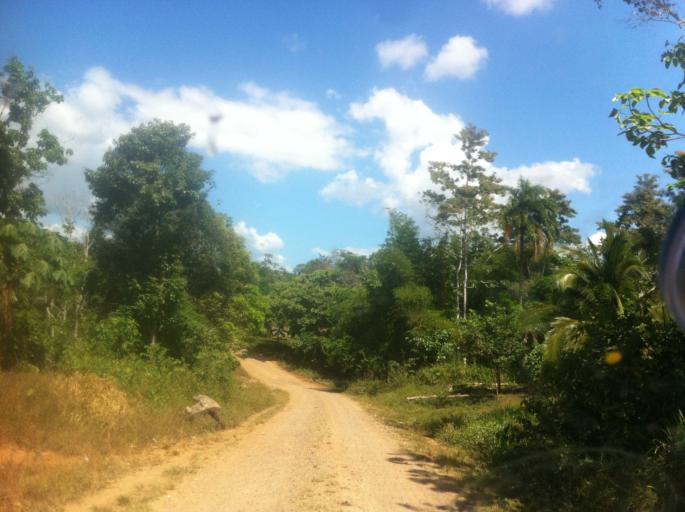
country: CR
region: Alajuela
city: Los Chiles
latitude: 11.2344
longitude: -84.4851
